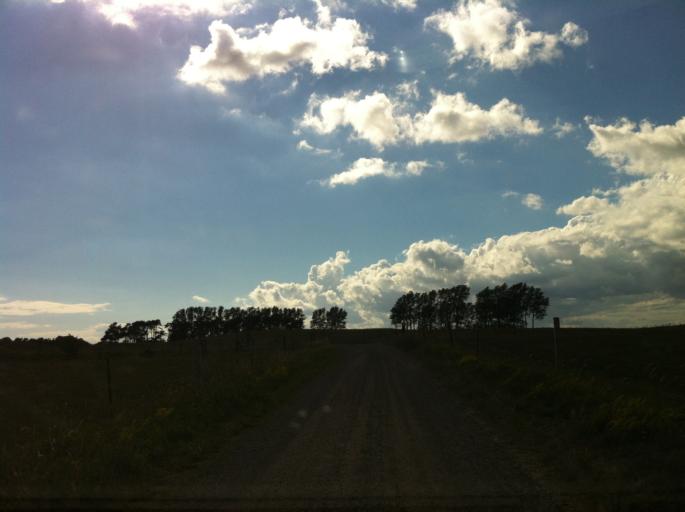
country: SE
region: Skane
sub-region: Ystads Kommun
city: Kopingebro
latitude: 55.3911
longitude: 14.0497
